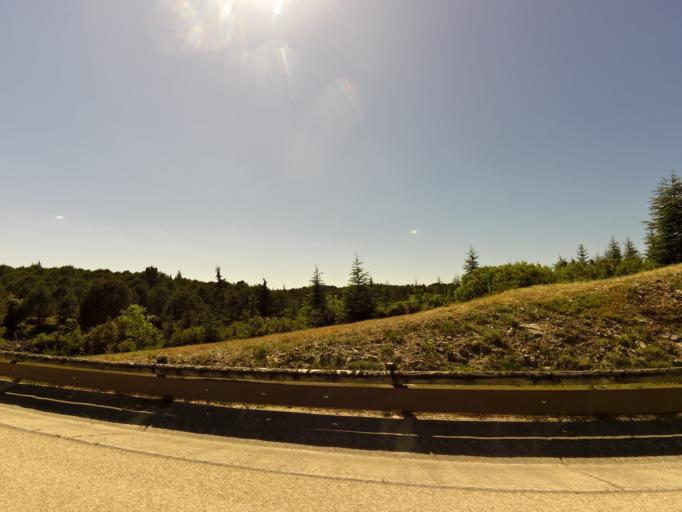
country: FR
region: Languedoc-Roussillon
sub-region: Departement de l'Herault
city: Teyran
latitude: 43.6993
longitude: 3.9431
